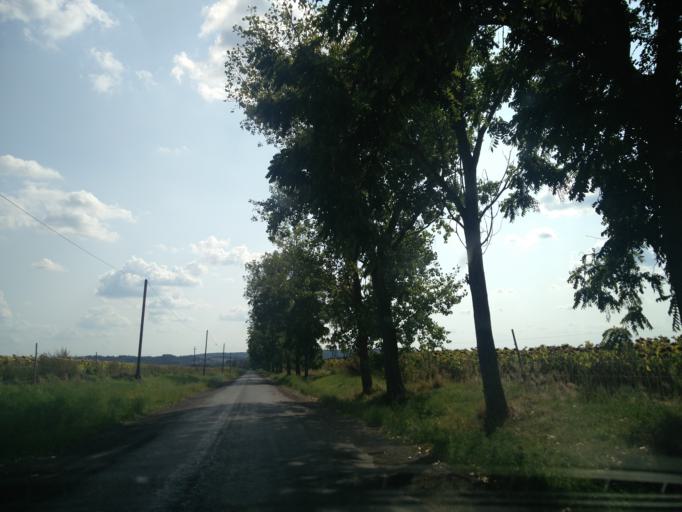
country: HU
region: Zala
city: Zalaegerszeg
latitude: 46.8920
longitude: 16.7594
